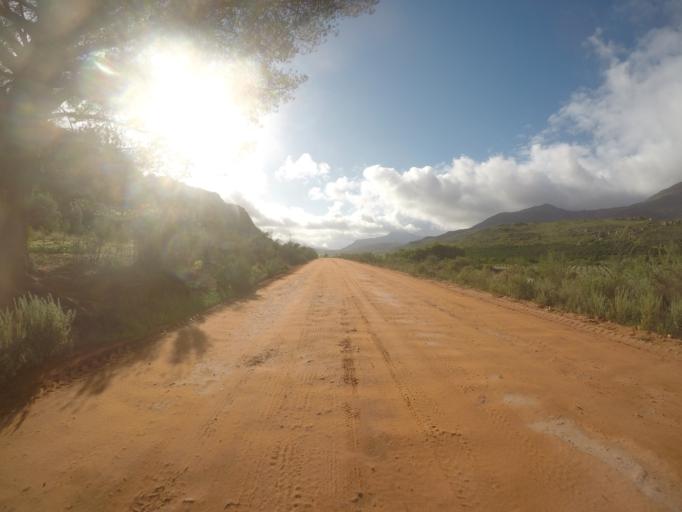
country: ZA
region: Western Cape
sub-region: West Coast District Municipality
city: Clanwilliam
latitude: -32.3428
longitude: 18.8097
